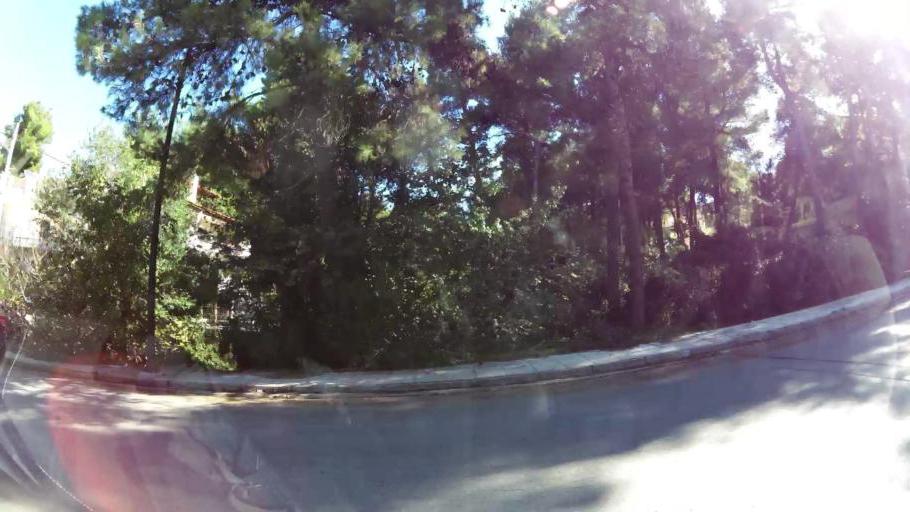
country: GR
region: Attica
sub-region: Nomarchia Anatolikis Attikis
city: Drosia
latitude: 38.1072
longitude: 23.8655
